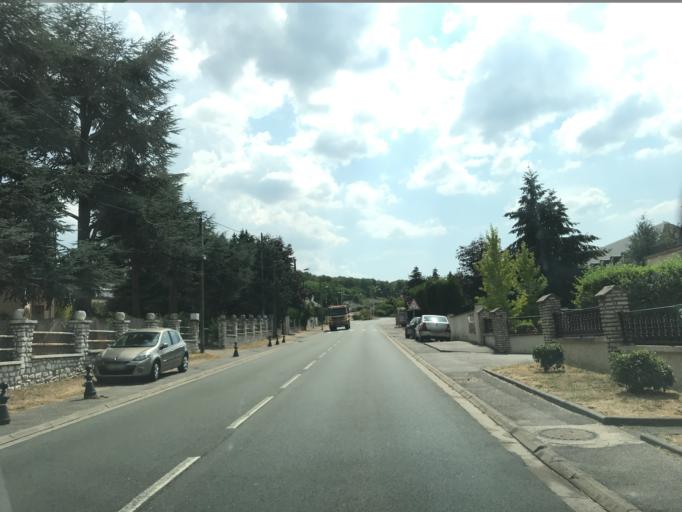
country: FR
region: Centre
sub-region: Departement d'Eure-et-Loir
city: Anet
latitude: 48.8492
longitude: 1.4341
